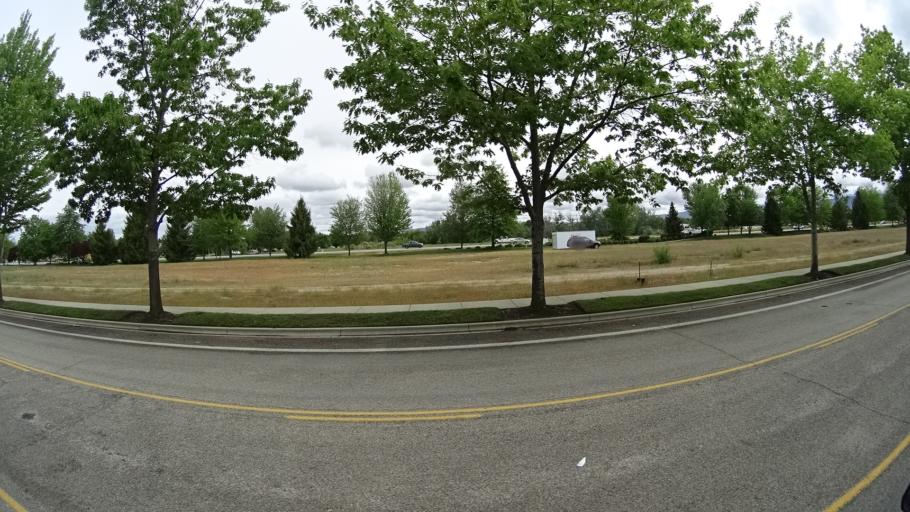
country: US
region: Idaho
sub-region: Ada County
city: Eagle
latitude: 43.6895
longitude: -116.3498
